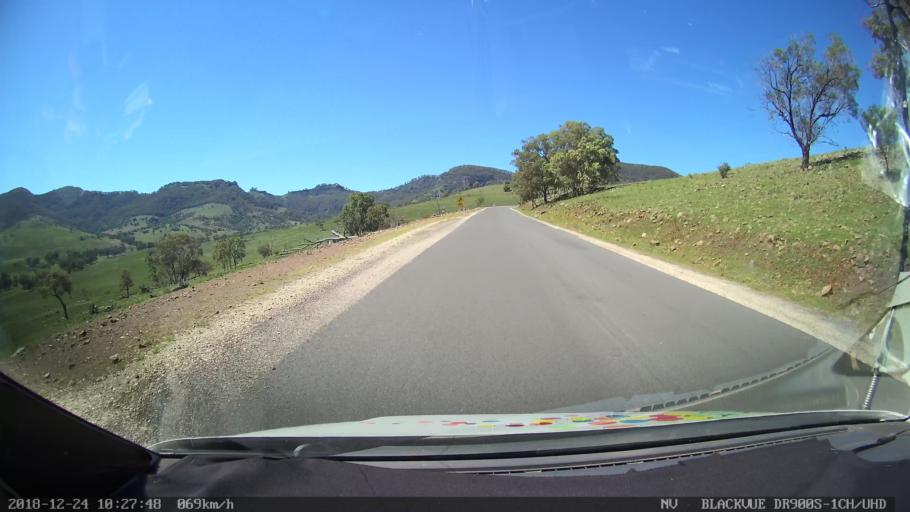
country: AU
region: New South Wales
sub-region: Liverpool Plains
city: Quirindi
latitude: -31.8211
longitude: 150.5337
